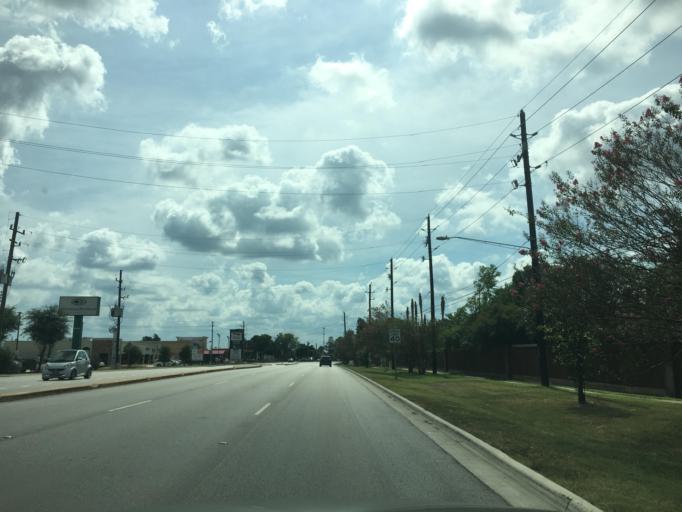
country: US
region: Texas
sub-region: Harris County
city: Spring
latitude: 30.1218
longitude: -95.4012
